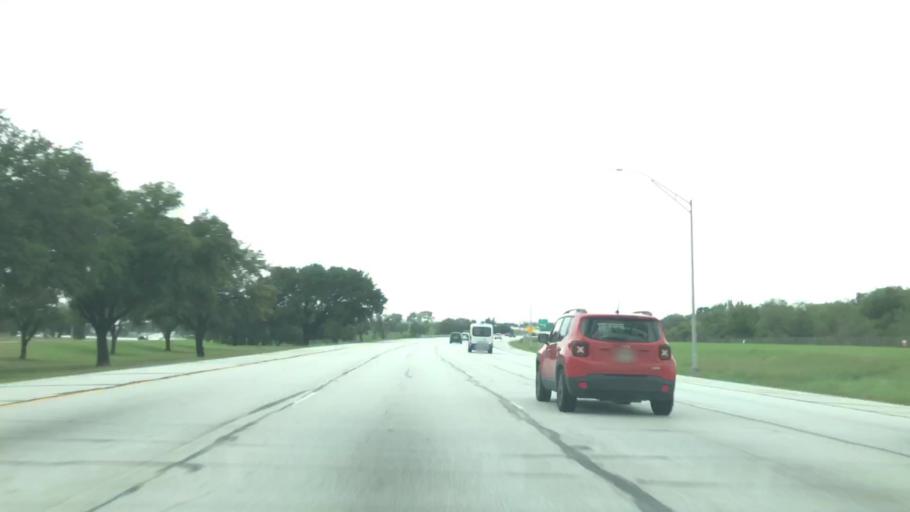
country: US
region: Texas
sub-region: Tarrant County
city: Euless
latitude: 32.8455
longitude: -97.0409
